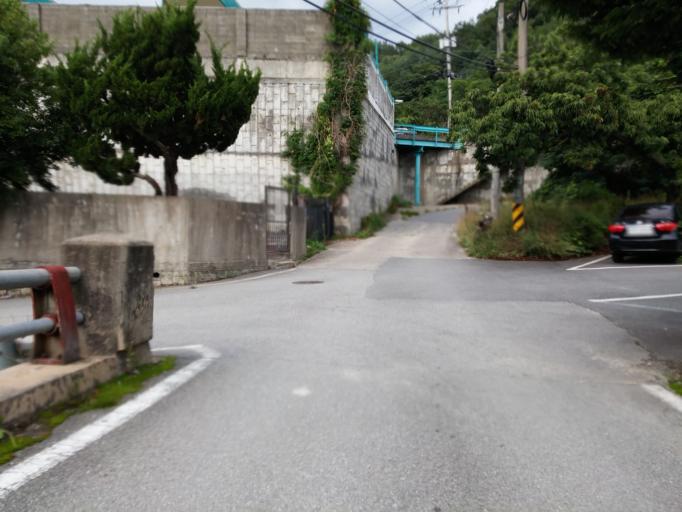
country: KR
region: Daejeon
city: Songgang-dong
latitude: 36.3664
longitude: 127.2659
